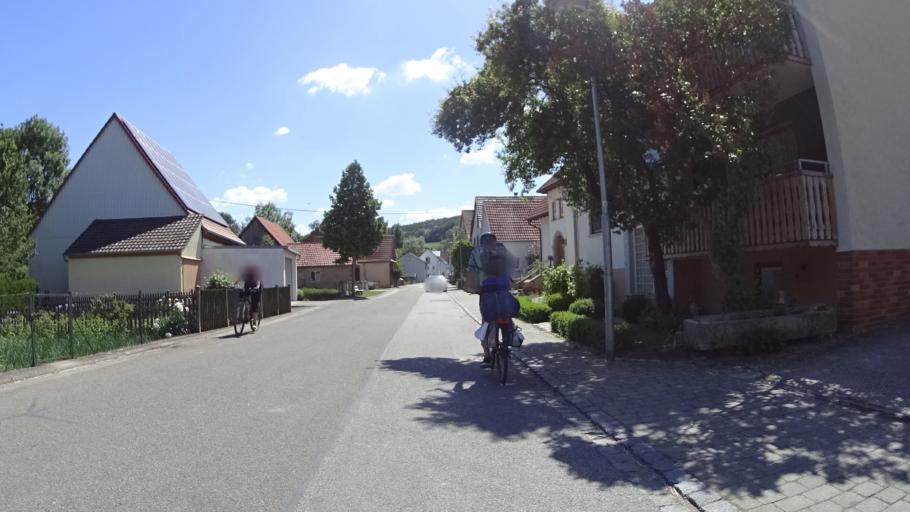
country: DE
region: Bavaria
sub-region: Regierungsbezirk Unterfranken
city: Tauberrettersheim
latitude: 49.4947
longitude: 9.9380
